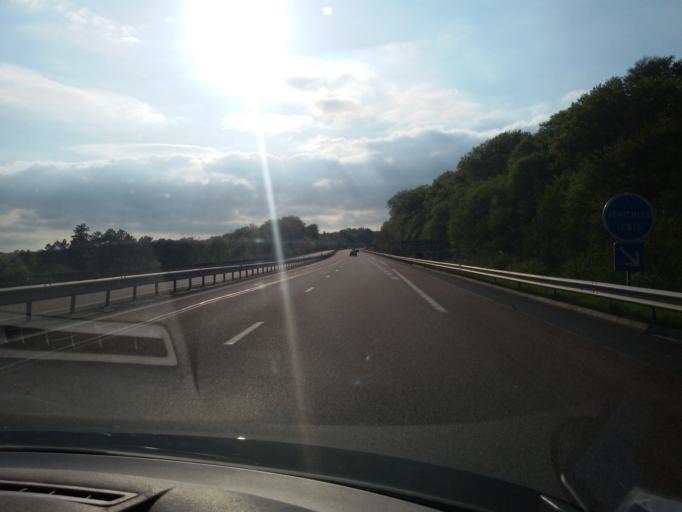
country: FR
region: Champagne-Ardenne
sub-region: Departement de l'Aube
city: Bar-sur-Aube
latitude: 48.1382
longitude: 4.6356
